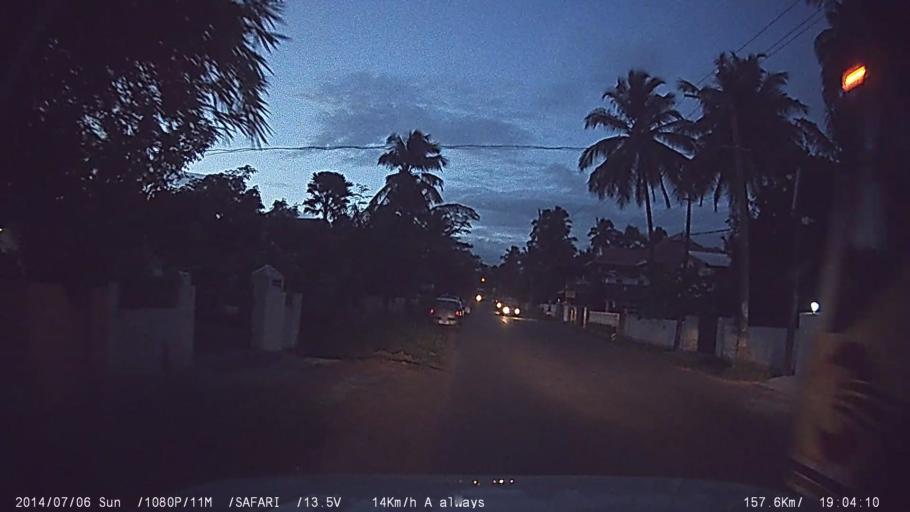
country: IN
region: Kerala
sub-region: Palakkad district
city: Palakkad
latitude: 10.7418
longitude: 76.6467
